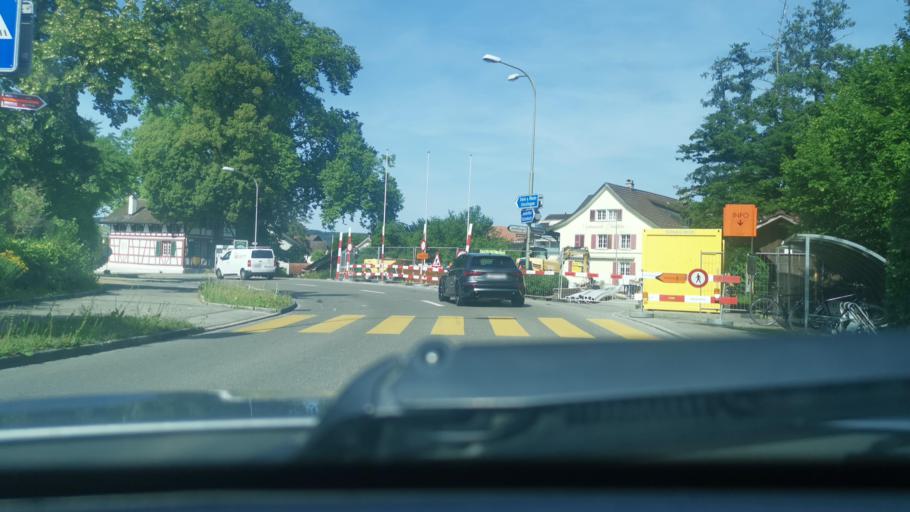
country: CH
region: Thurgau
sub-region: Frauenfeld District
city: Gachnang
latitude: 47.5628
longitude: 8.8243
